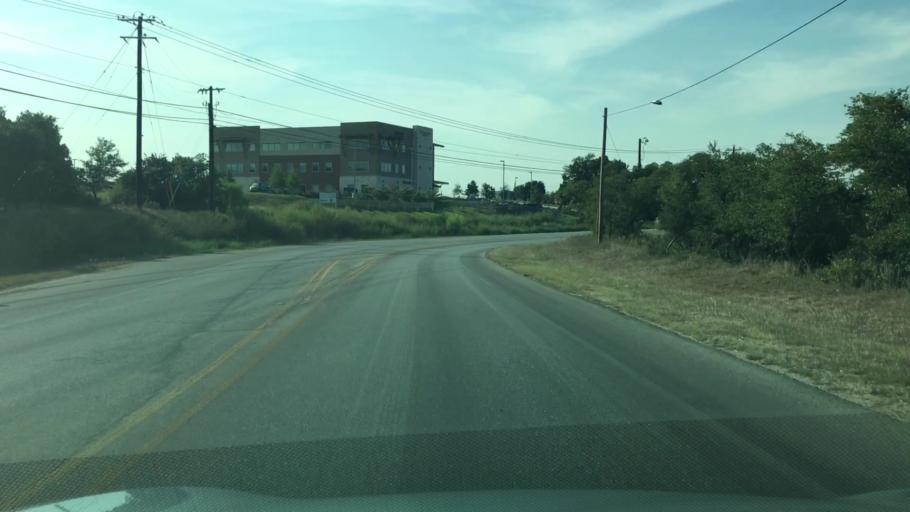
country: US
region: Texas
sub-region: Hays County
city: Dripping Springs
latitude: 30.1934
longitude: -97.9975
